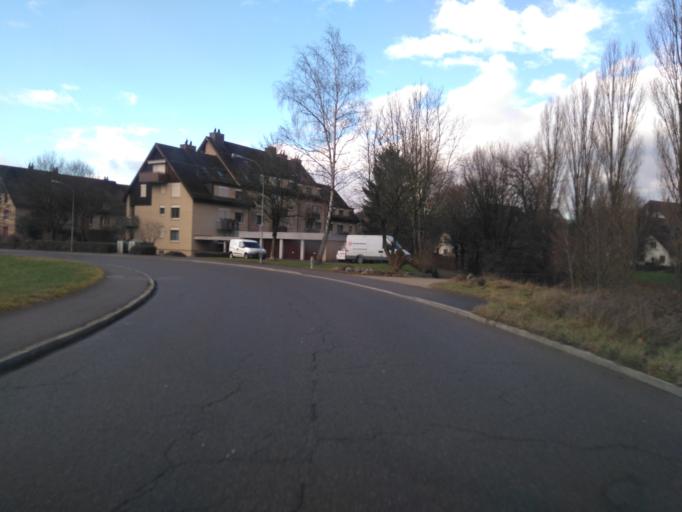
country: CH
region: Zurich
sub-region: Bezirk Dielsdorf
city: Regensdorf / Feldblumen-Riedthofstrasse
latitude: 47.4443
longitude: 8.4696
